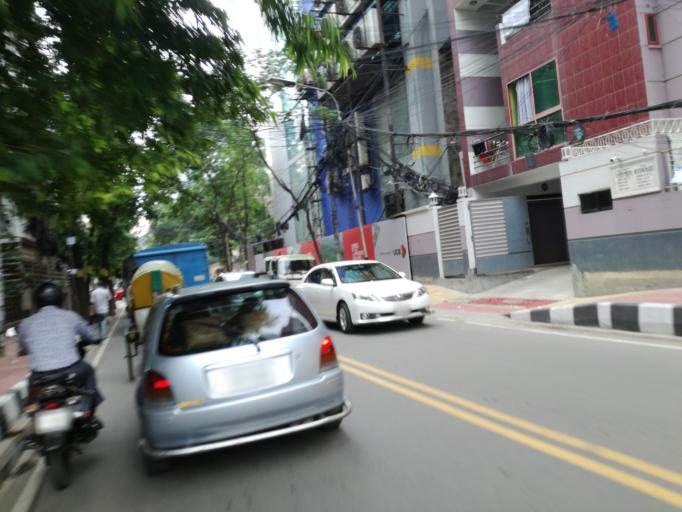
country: BD
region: Dhaka
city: Paltan
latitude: 23.7871
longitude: 90.4161
